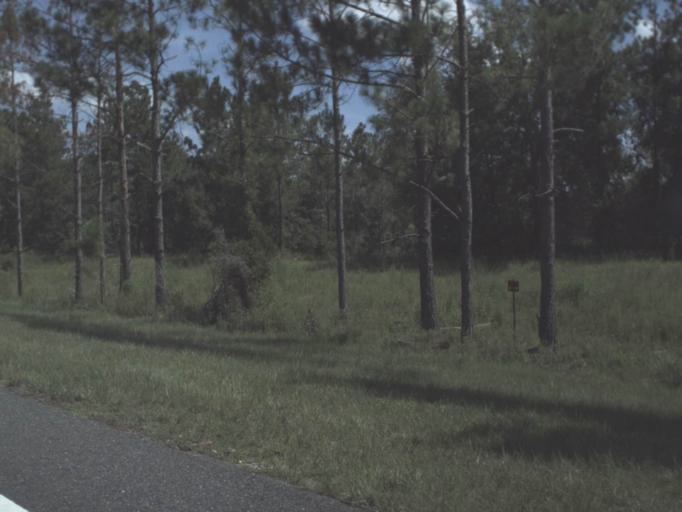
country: US
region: Florida
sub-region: Levy County
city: Chiefland
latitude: 29.4268
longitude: -82.8292
